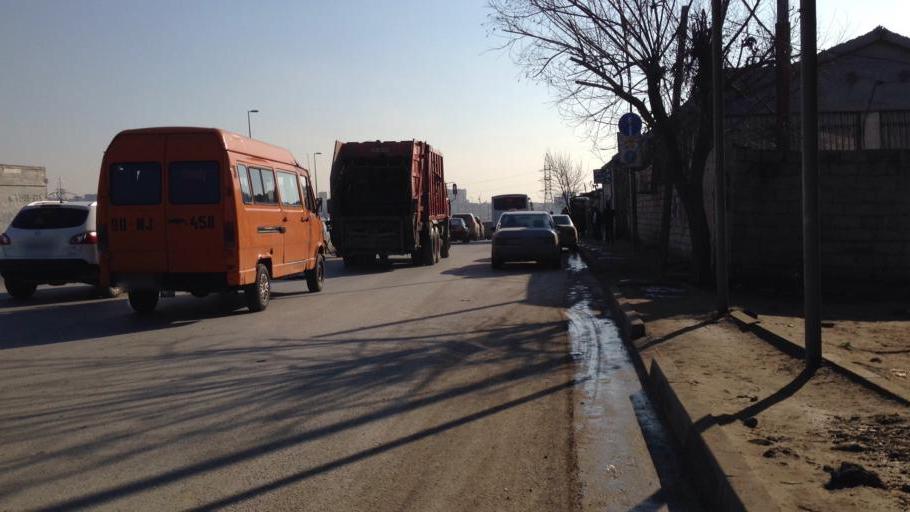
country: AZ
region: Baki
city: Sabuncu
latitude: 40.4429
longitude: 49.9336
